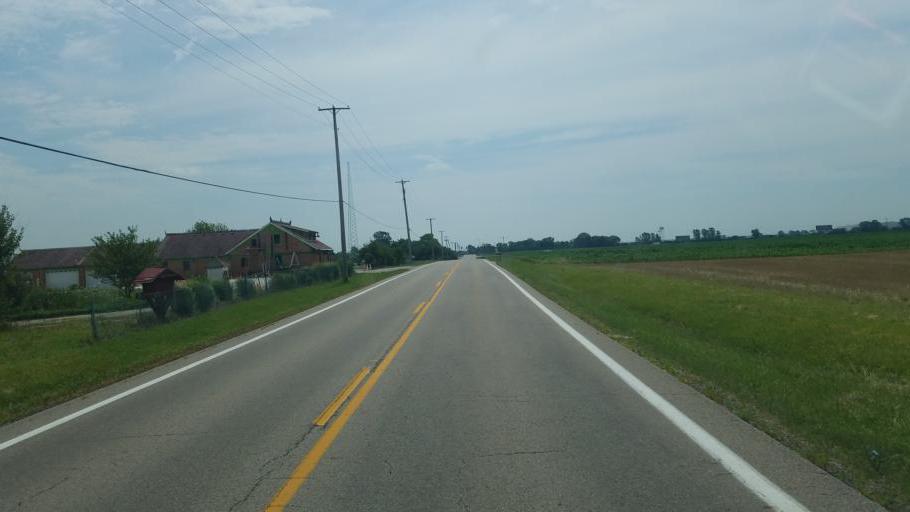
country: US
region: Ohio
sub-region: Madison County
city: West Jefferson
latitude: 39.9688
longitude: -83.3669
